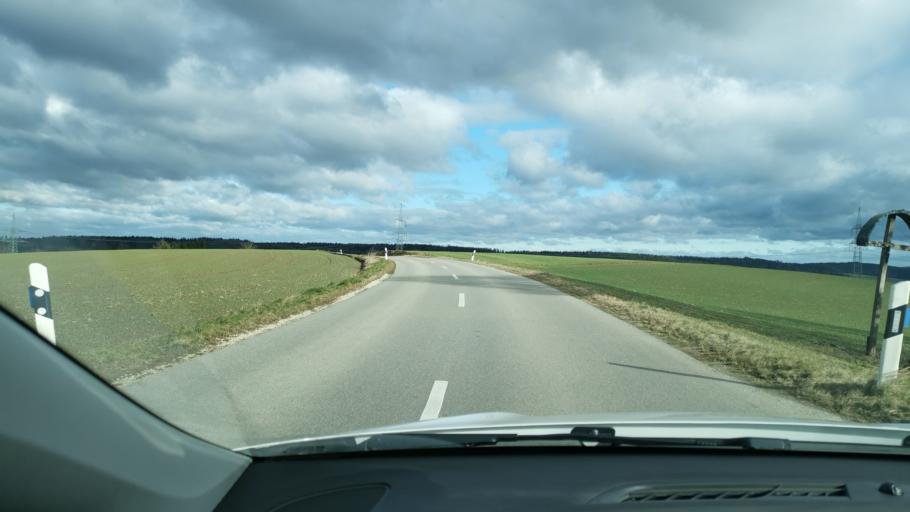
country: DE
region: Bavaria
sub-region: Swabia
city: Aindling
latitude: 48.5213
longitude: 10.9530
